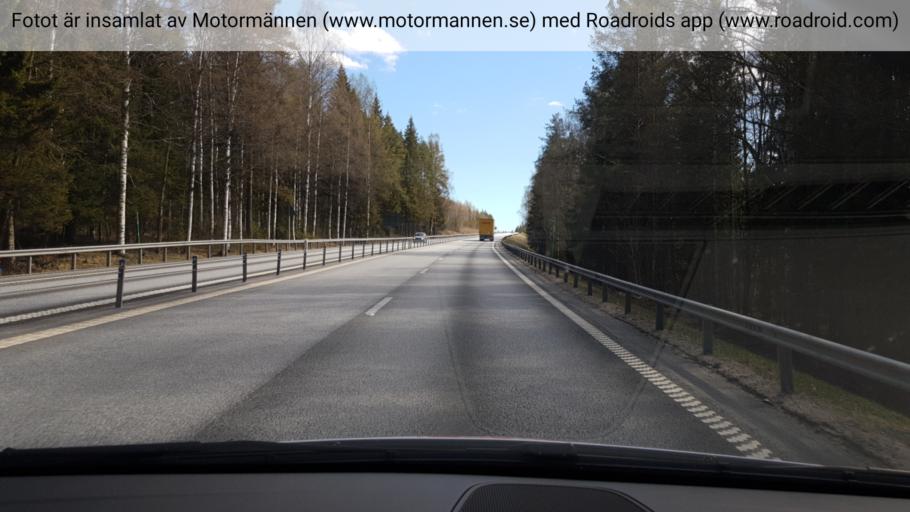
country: SE
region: Vaesterbotten
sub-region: Vannas Kommun
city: Vannasby
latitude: 63.9104
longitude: 19.8874
